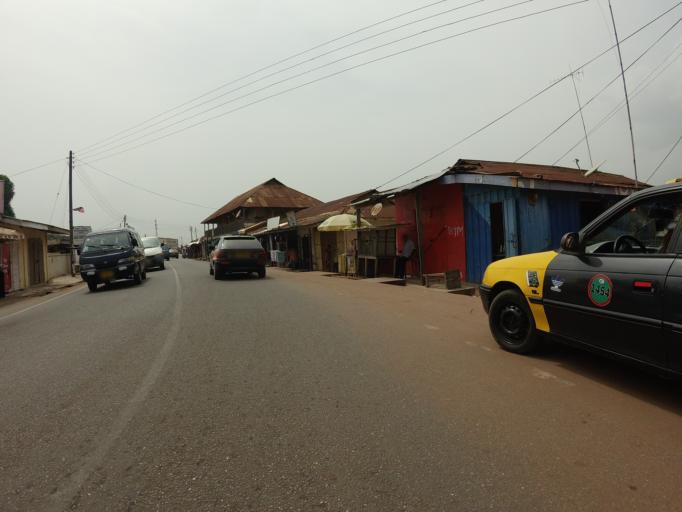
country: GH
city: Akropong
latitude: 6.1043
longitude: -0.0150
